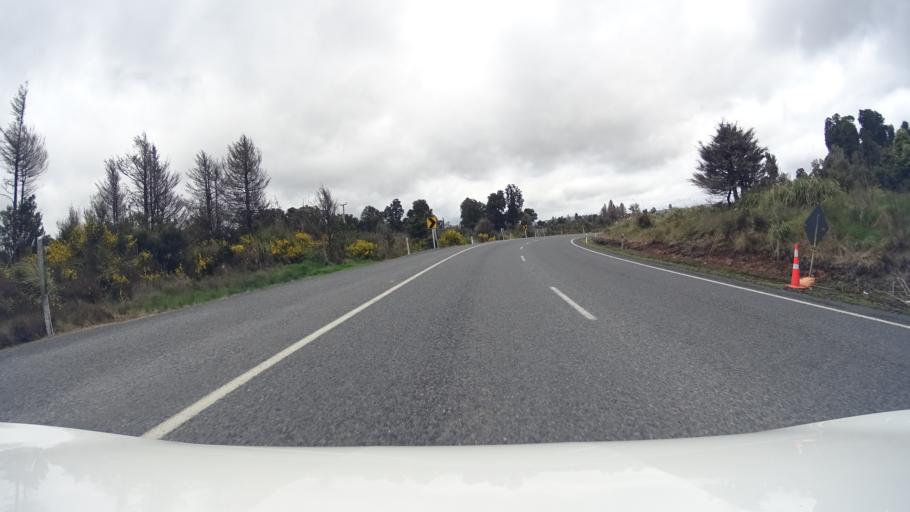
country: NZ
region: Manawatu-Wanganui
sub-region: Ruapehu District
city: Waiouru
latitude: -39.2638
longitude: 175.3908
